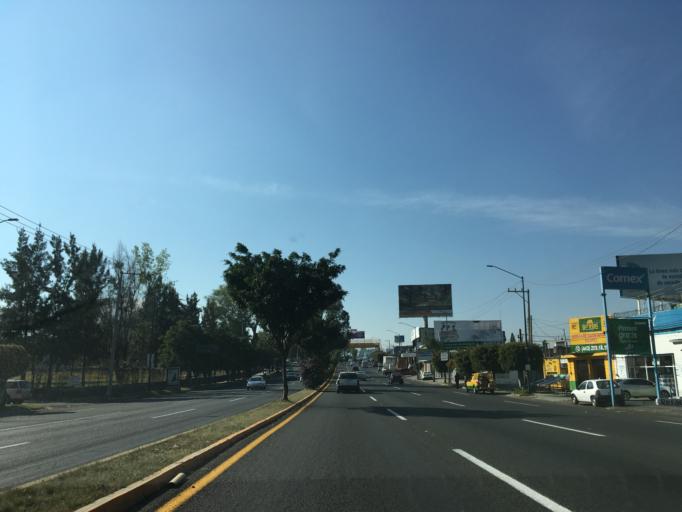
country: MX
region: Michoacan
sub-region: Tarimbaro
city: Fraccionamiento Privadas del Sol
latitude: 19.7298
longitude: -101.1831
